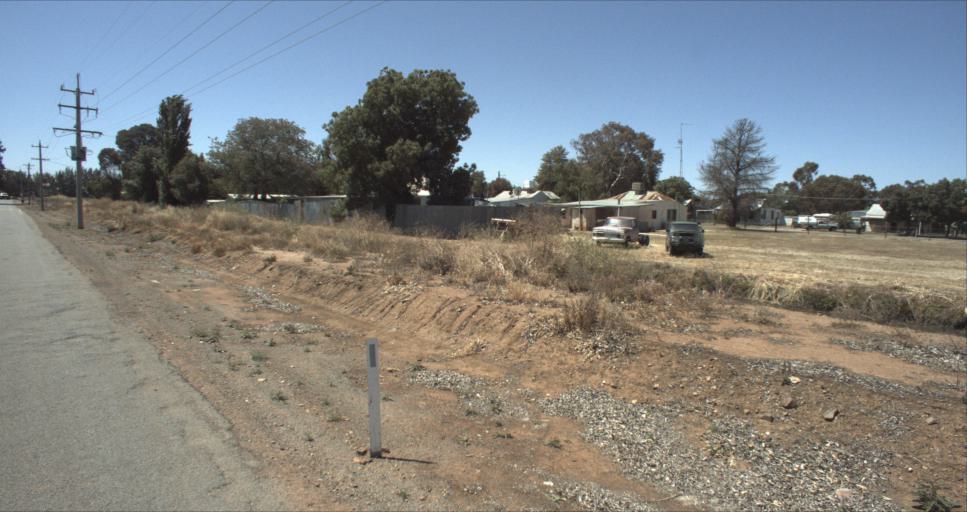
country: AU
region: New South Wales
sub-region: Leeton
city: Leeton
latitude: -34.5249
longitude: 146.3301
